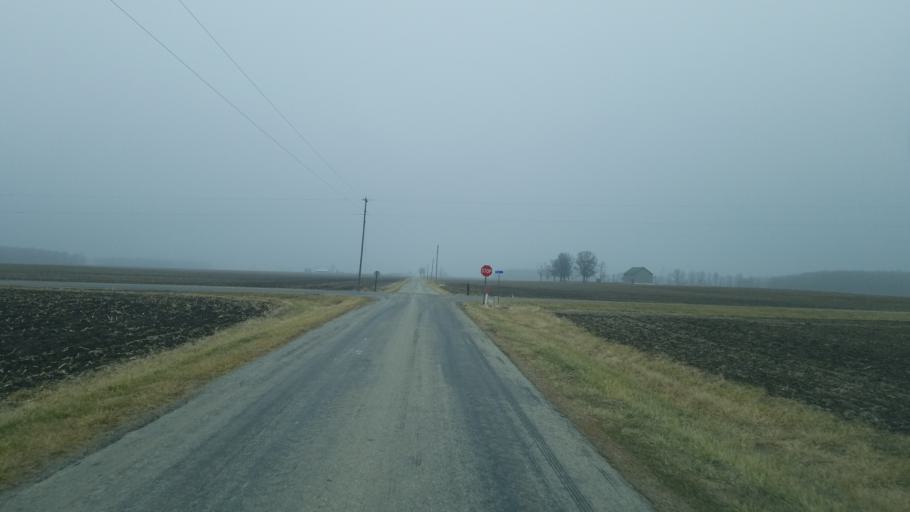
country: US
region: Indiana
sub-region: Wells County
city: Bluffton
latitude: 40.6103
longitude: -85.1071
